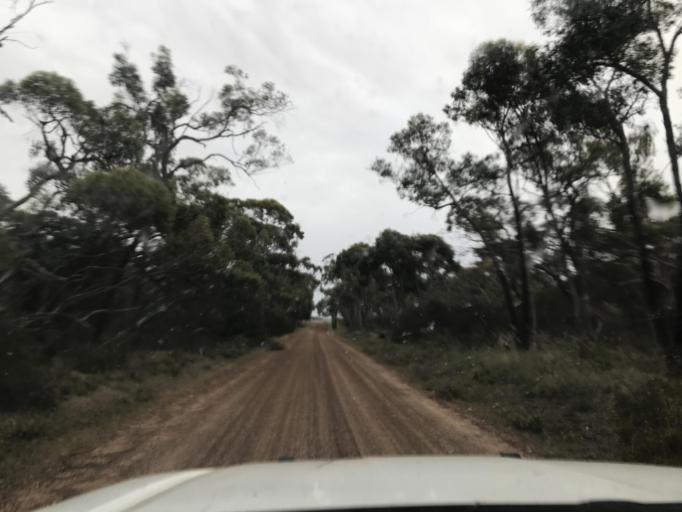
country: AU
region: South Australia
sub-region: Wattle Range
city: Penola
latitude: -37.0907
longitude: 141.4992
